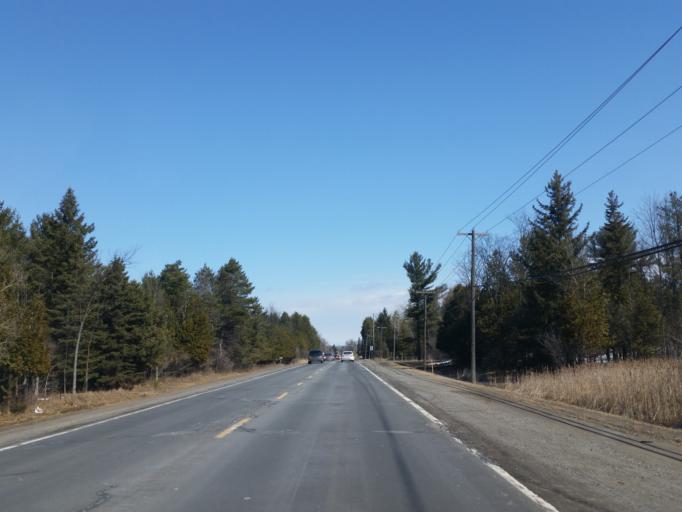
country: CA
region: Ontario
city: Bells Corners
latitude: 45.3058
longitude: -75.8310
